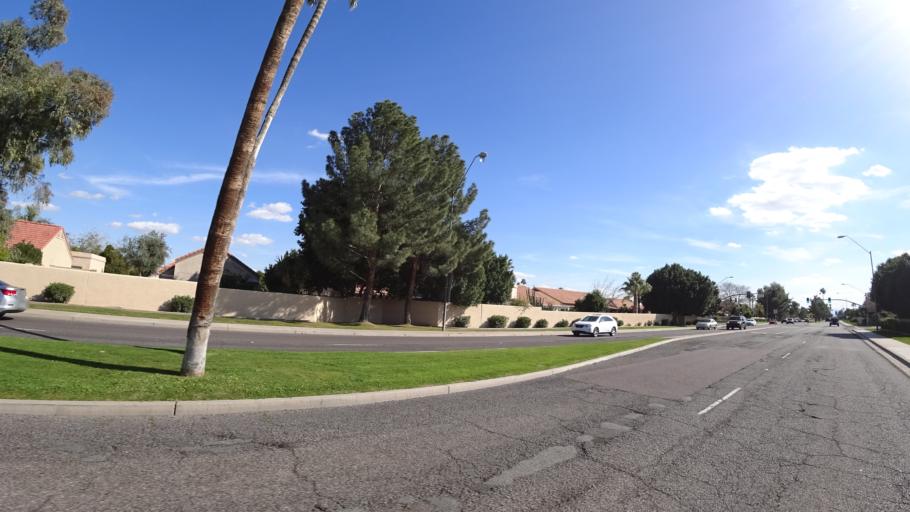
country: US
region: Arizona
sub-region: Maricopa County
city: Sun City
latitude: 33.6610
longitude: -112.2206
